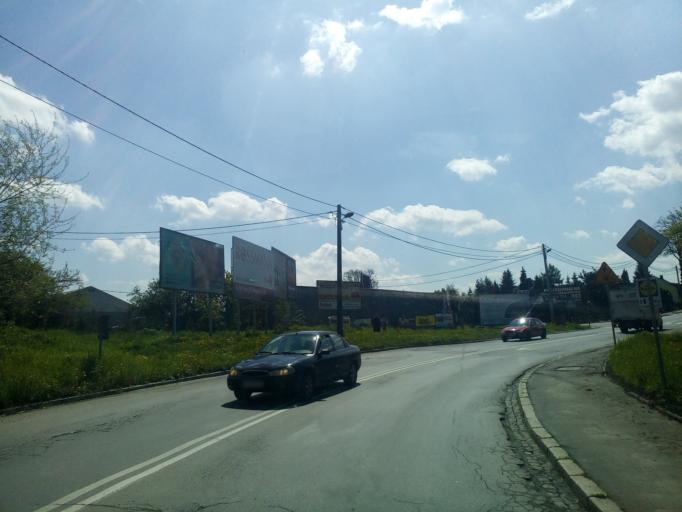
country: PL
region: Lesser Poland Voivodeship
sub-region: Powiat nowosadecki
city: Nowy Sacz
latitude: 49.6008
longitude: 20.6859
